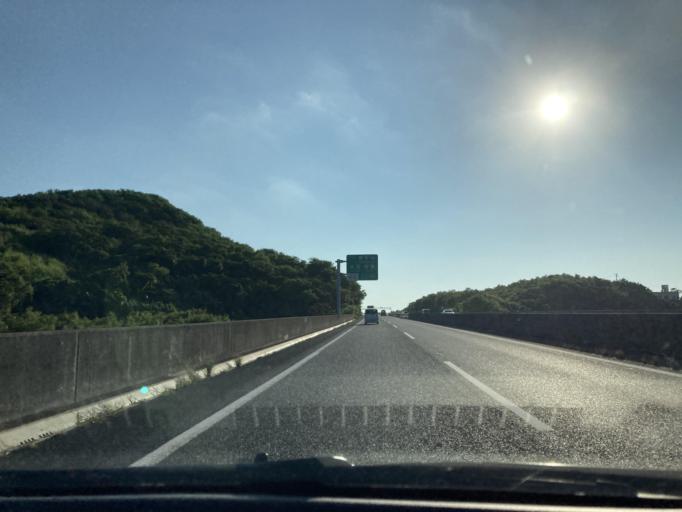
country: JP
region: Okinawa
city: Tomigusuku
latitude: 26.1772
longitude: 127.7104
